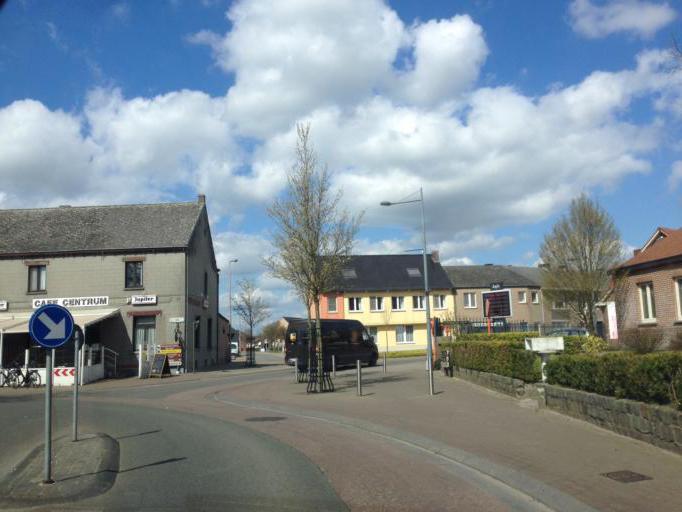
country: BE
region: Flanders
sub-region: Provincie Limburg
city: Bree
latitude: 51.1551
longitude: 5.6028
